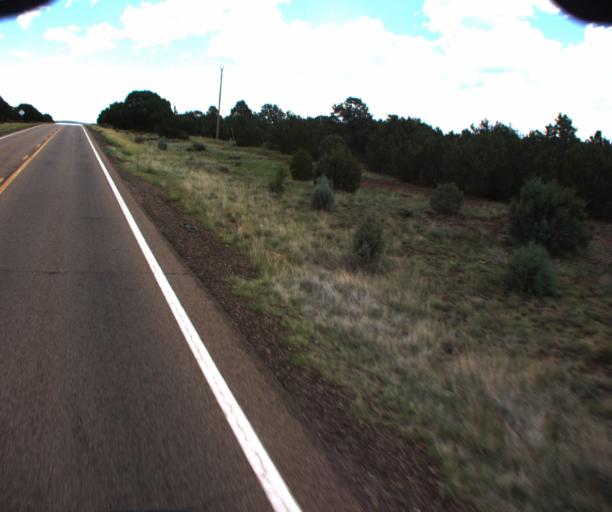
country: US
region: Arizona
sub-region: Navajo County
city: White Mountain Lake
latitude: 34.2814
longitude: -109.8080
